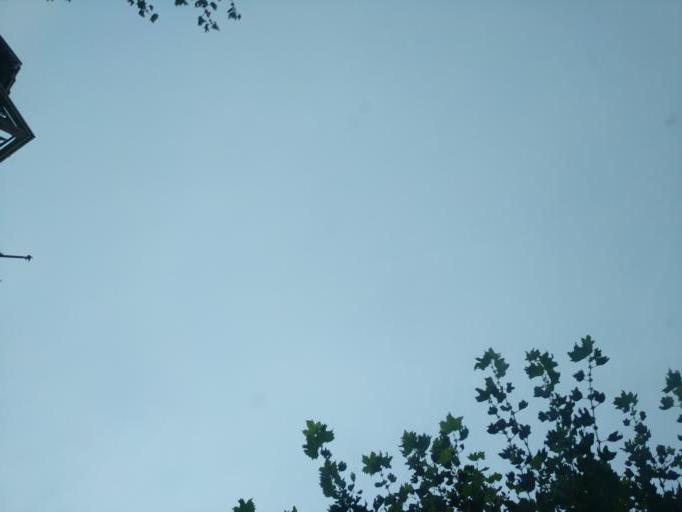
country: ES
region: Asturias
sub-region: Province of Asturias
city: Aviles
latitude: 43.5742
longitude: -5.9608
